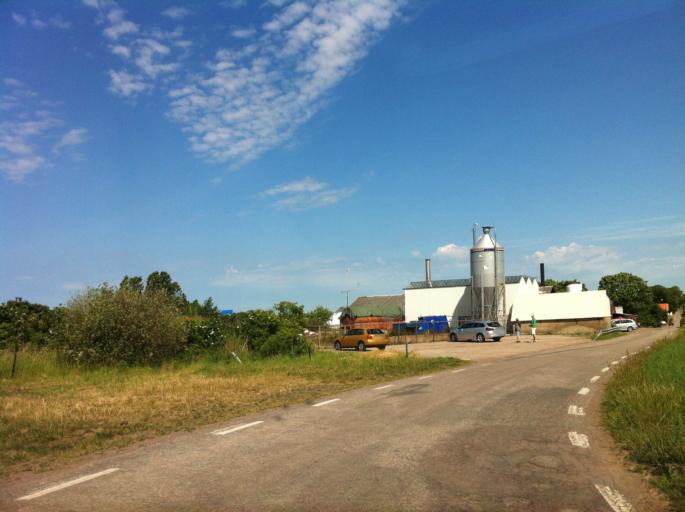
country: SE
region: Skane
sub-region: Helsingborg
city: Glumslov
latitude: 55.9446
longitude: 12.8806
